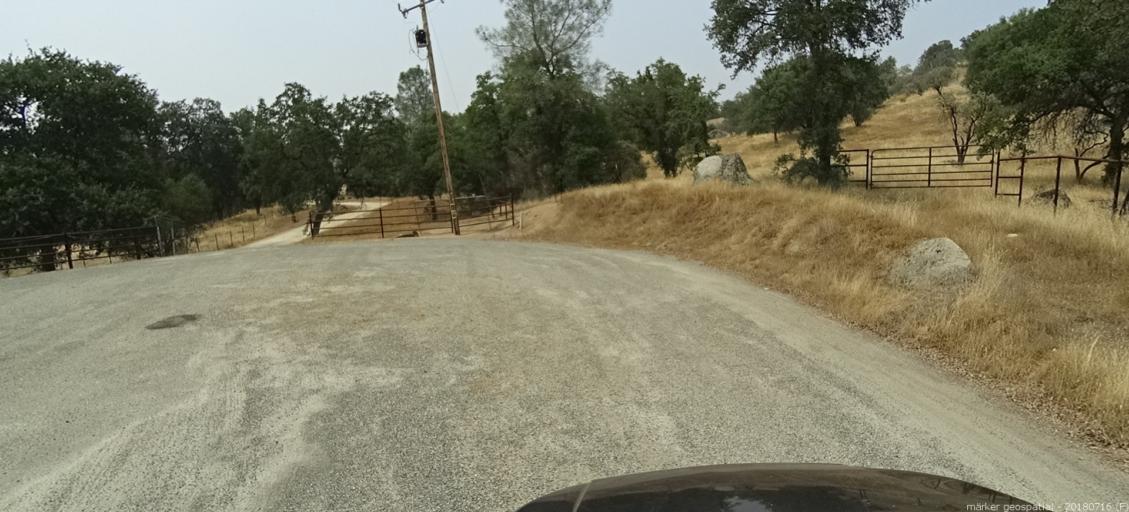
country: US
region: California
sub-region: Madera County
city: Yosemite Lakes
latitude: 37.2359
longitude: -119.8040
